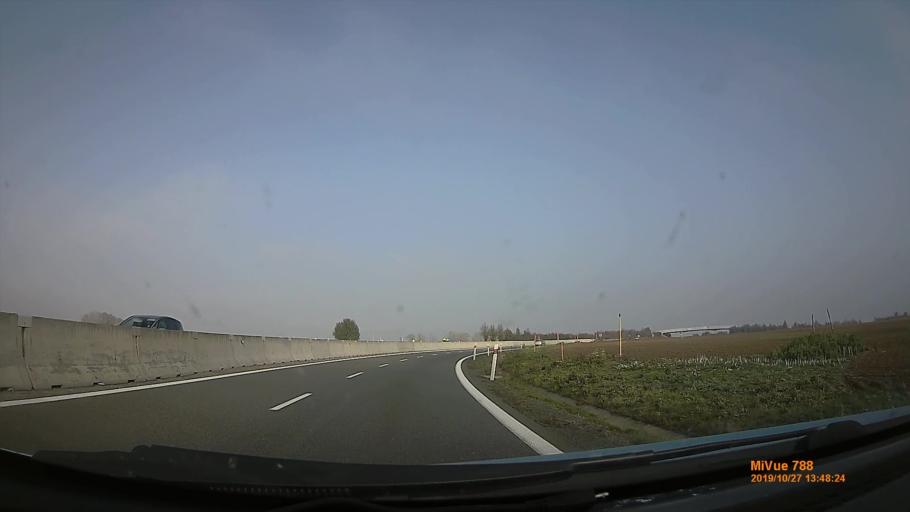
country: CZ
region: Olomoucky
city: Hnevotin
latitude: 49.6008
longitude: 17.1997
